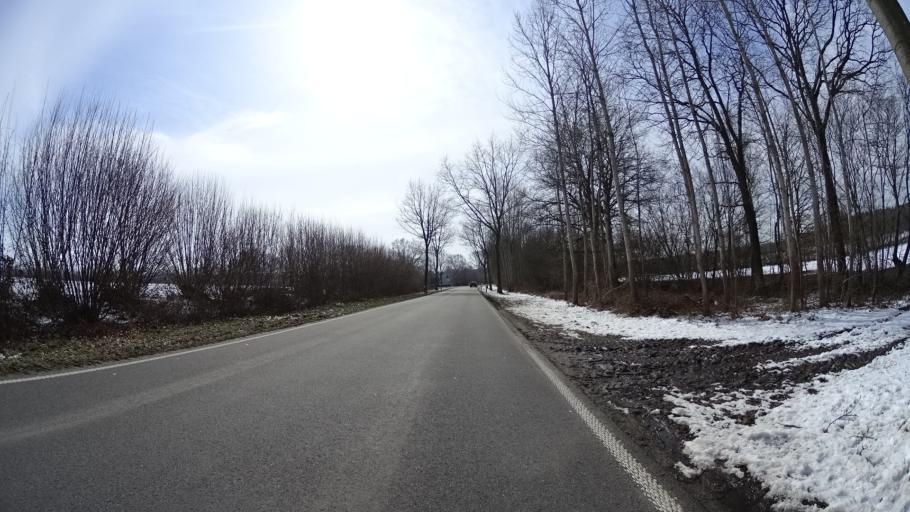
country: DE
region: Schleswig-Holstein
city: Latendorf
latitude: 54.0083
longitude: 10.0610
